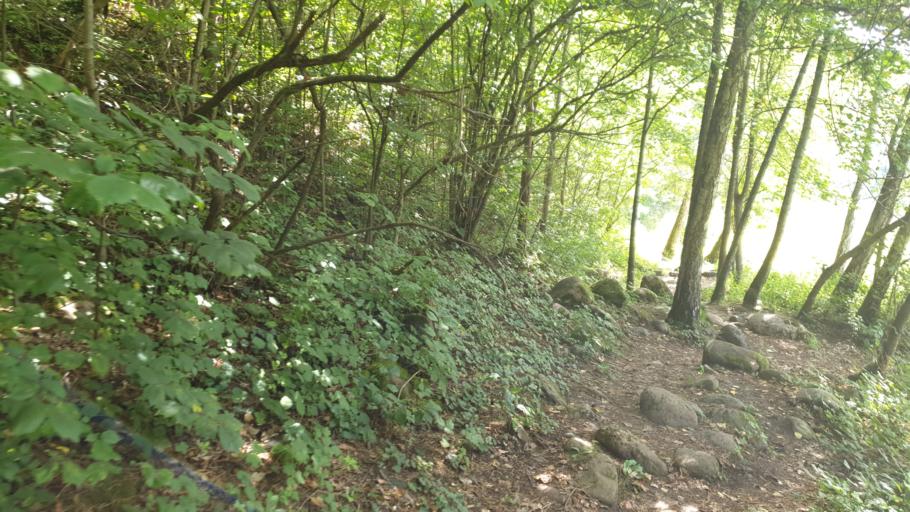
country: LT
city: Grigiskes
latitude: 54.8021
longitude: 24.9762
